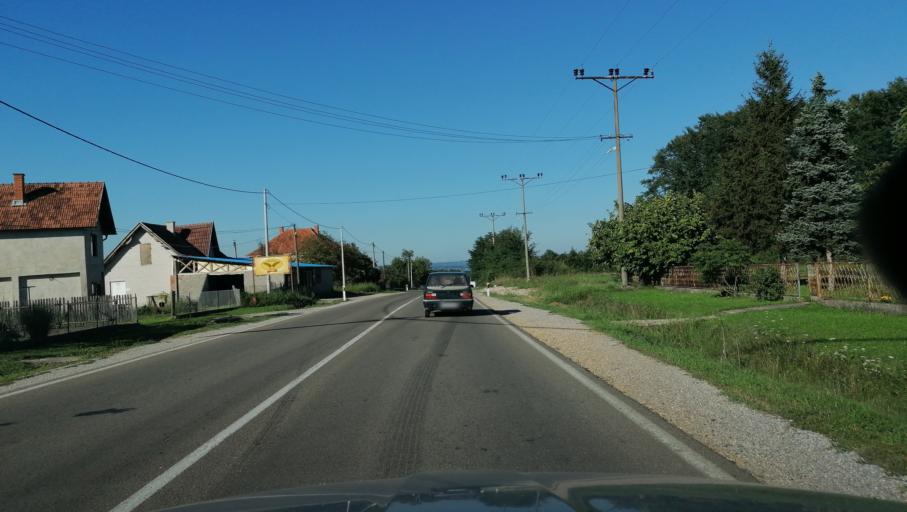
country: RS
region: Central Serbia
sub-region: Sumadijski Okrug
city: Knic
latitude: 43.9082
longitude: 20.6361
